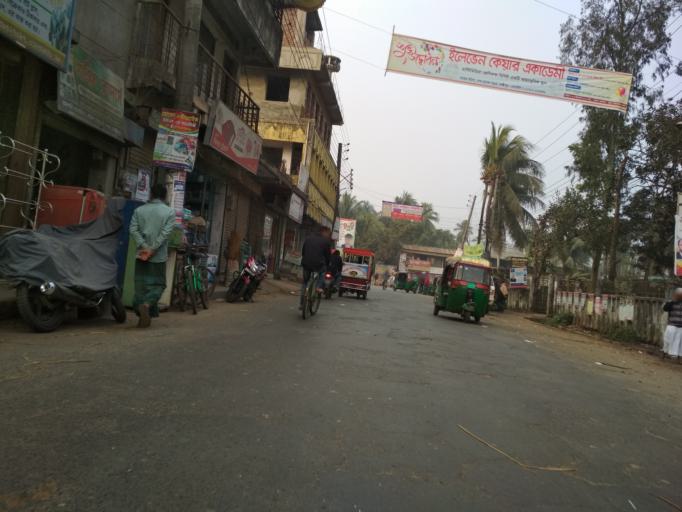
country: BD
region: Chittagong
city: Lakshmipur
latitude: 22.9320
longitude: 90.8333
